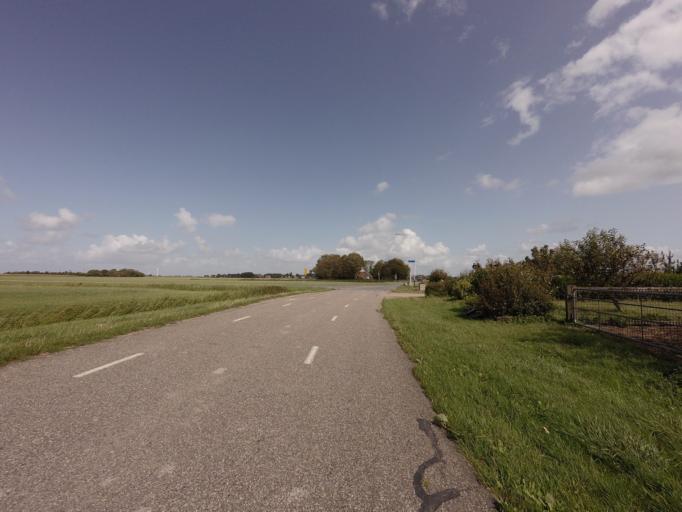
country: NL
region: Friesland
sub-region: Sudwest Fryslan
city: Makkum
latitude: 53.1075
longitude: 5.4327
